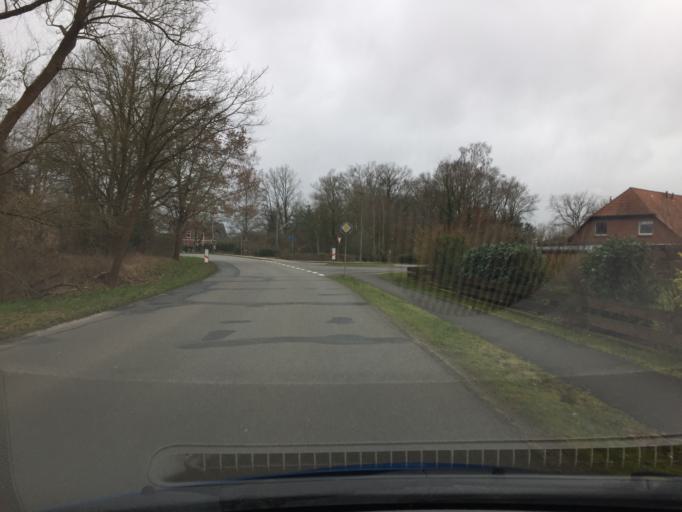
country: DE
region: Lower Saxony
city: Wrestedt
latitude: 52.9283
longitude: 10.5688
